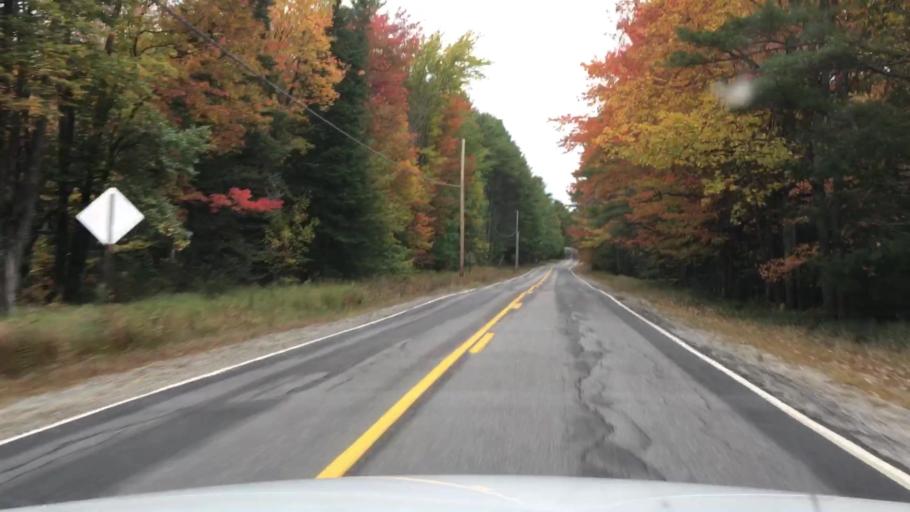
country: US
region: Maine
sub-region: Oxford County
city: Bethel
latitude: 44.3689
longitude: -70.8001
